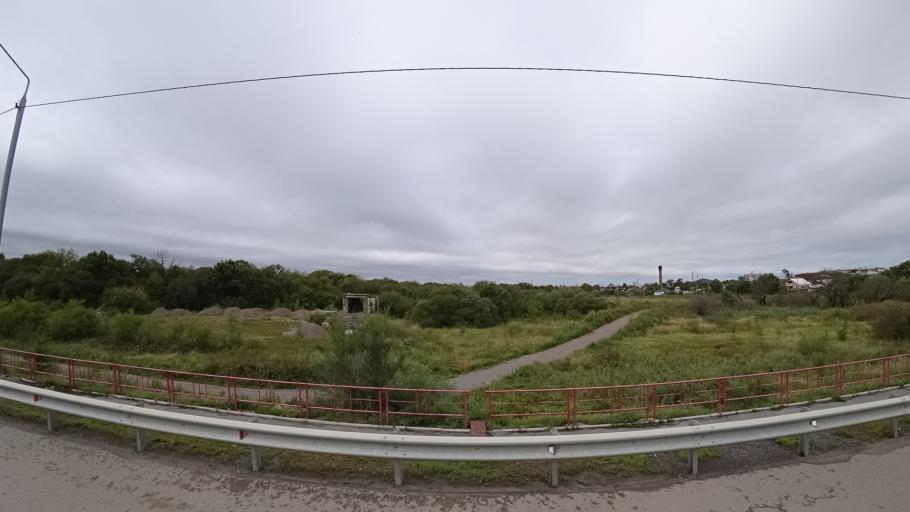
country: RU
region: Primorskiy
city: Monastyrishche
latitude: 44.1981
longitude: 132.4469
